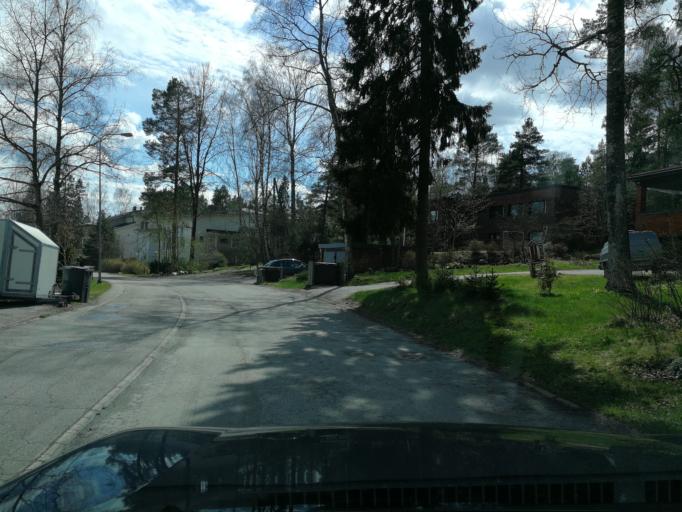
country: FI
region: Uusimaa
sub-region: Helsinki
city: Espoo
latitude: 60.1632
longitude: 24.6918
